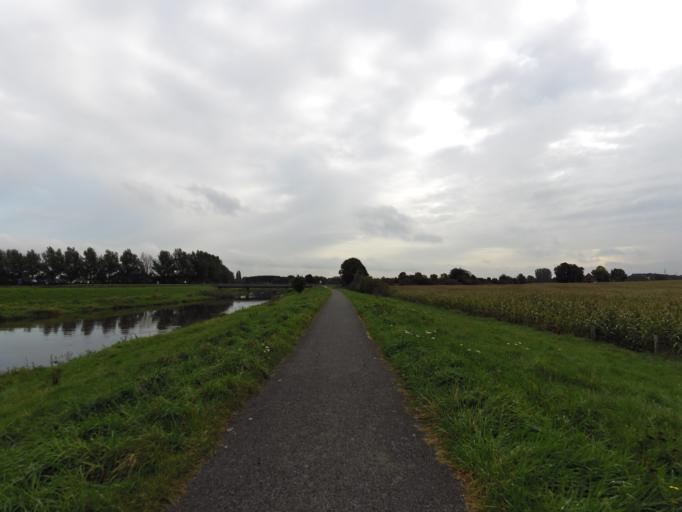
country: DE
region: North Rhine-Westphalia
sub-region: Regierungsbezirk Munster
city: Isselburg
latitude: 51.8559
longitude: 6.4622
